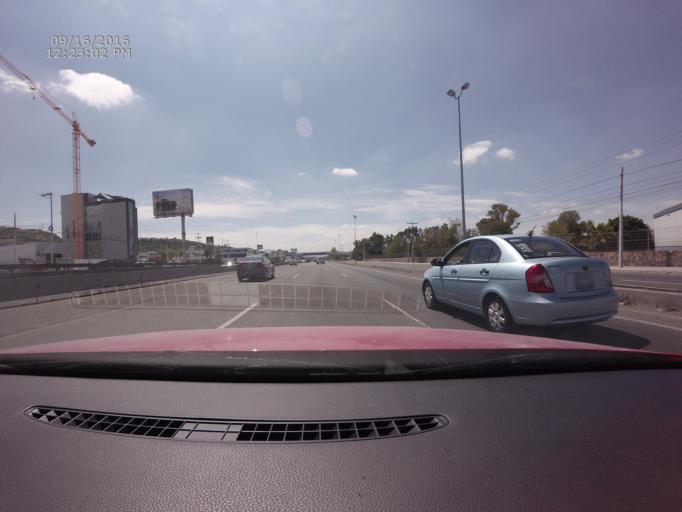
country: MX
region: Queretaro
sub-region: Queretaro
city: Sergio Villasenor
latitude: 20.6321
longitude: -100.4268
